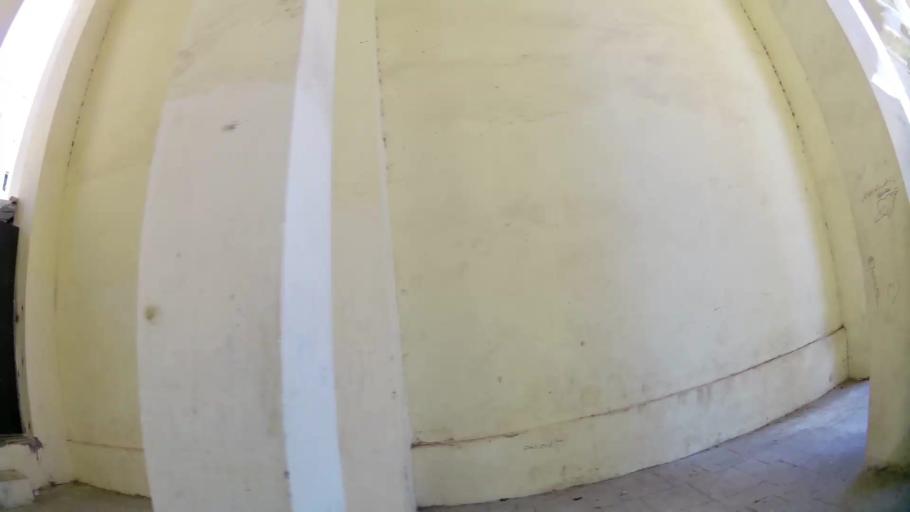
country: MA
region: Rabat-Sale-Zemmour-Zaer
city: Sale
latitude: 34.0813
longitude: -6.7823
